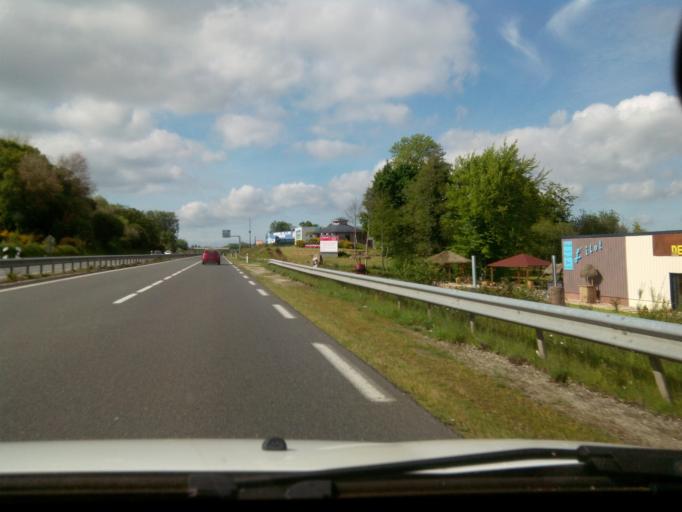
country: FR
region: Brittany
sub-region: Departement des Cotes-d'Armor
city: Begard
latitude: 48.6388
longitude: -3.3246
